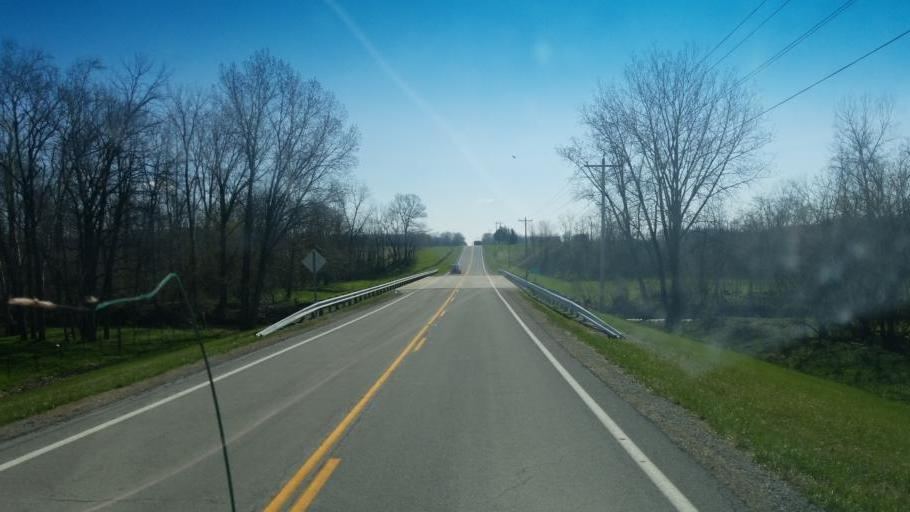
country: US
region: Ohio
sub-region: Hardin County
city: Forest
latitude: 40.7374
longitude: -83.3985
